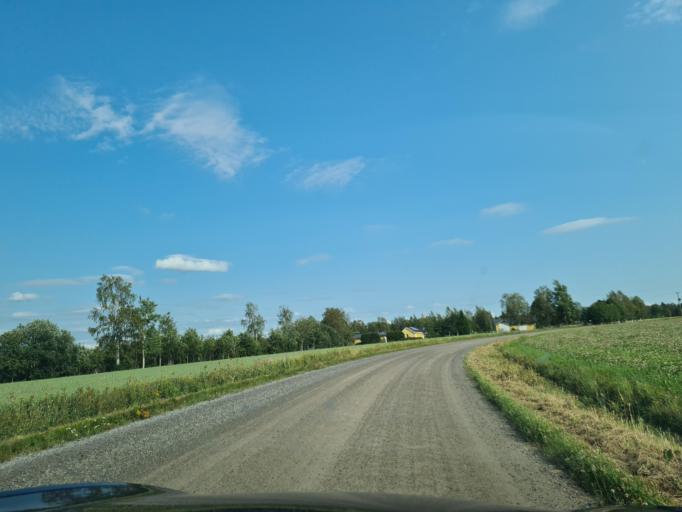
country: FI
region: Ostrobothnia
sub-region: Kyroenmaa
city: Laihia
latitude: 63.0300
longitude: 21.8932
